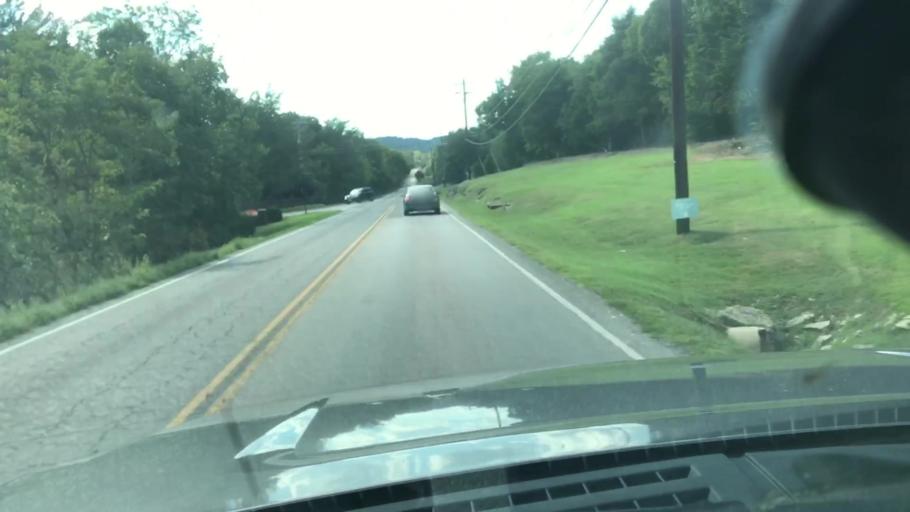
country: US
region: Tennessee
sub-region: Davidson County
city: Forest Hills
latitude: 36.0260
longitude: -86.8955
